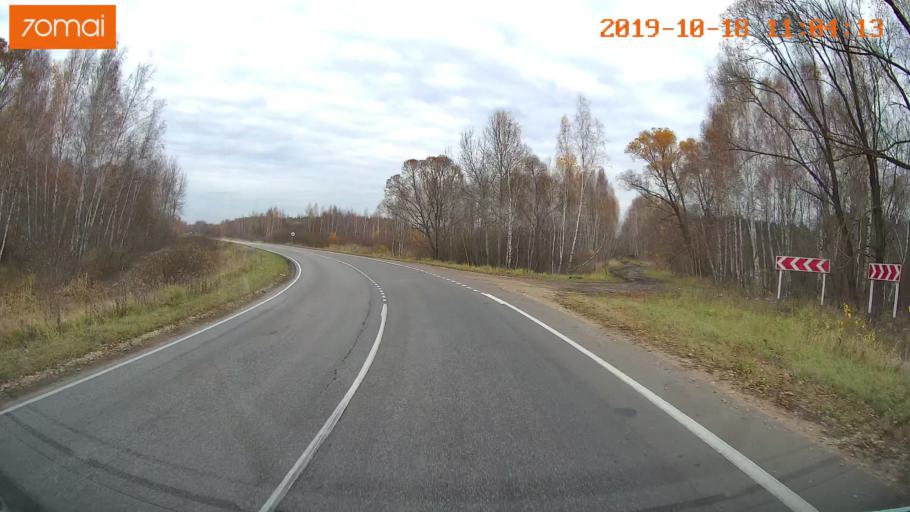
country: RU
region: Tula
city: Yepifan'
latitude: 53.8913
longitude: 38.5504
